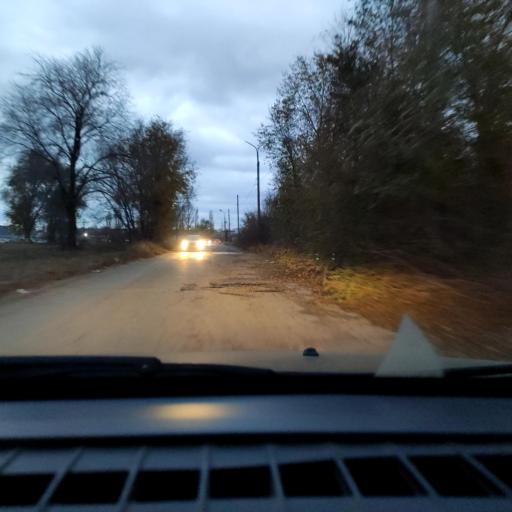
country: RU
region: Samara
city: Tol'yatti
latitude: 53.5614
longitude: 49.3125
